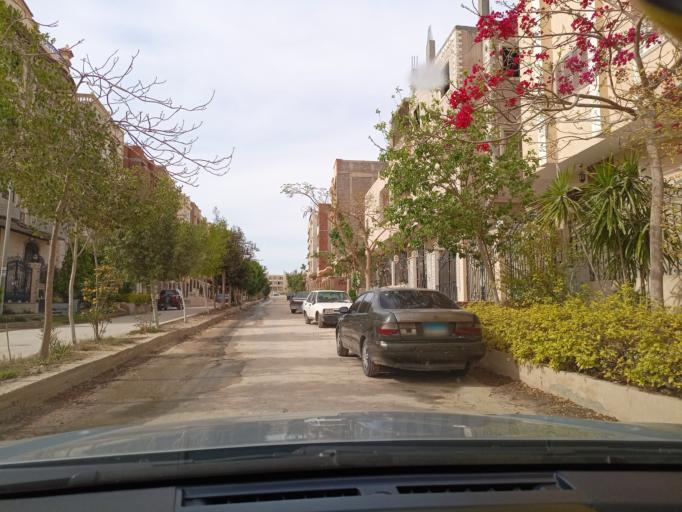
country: EG
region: Muhafazat al Qalyubiyah
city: Al Khankah
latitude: 30.2584
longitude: 31.4786
